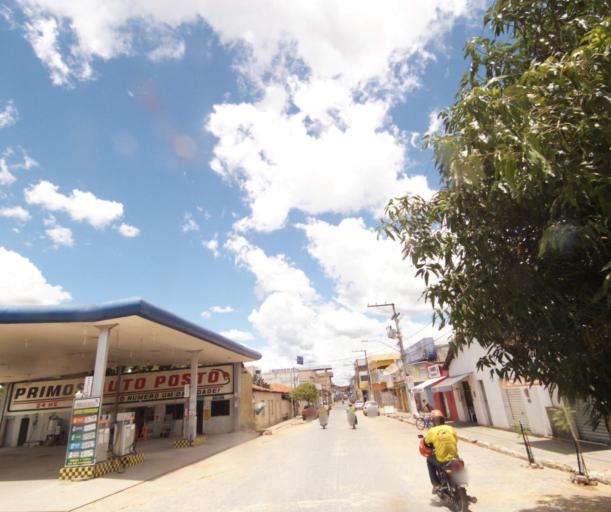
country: BR
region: Bahia
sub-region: Sao Felix Do Coribe
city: Santa Maria da Vitoria
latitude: -13.3976
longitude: -44.2020
